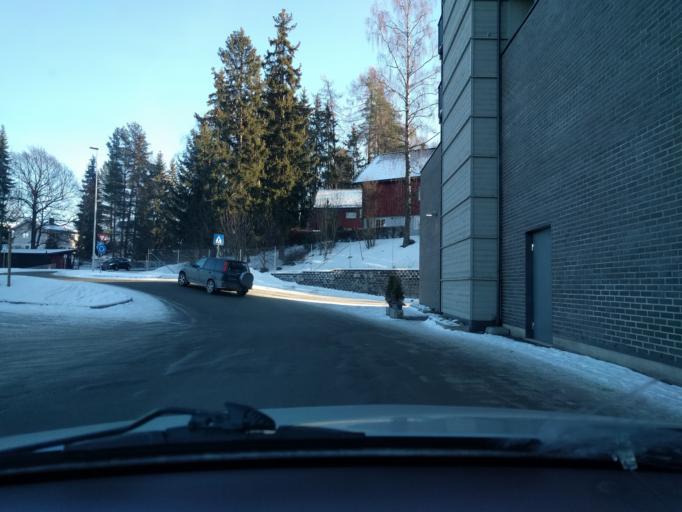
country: NO
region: Hedmark
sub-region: Hamar
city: Hamar
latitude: 60.7974
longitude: 11.0508
